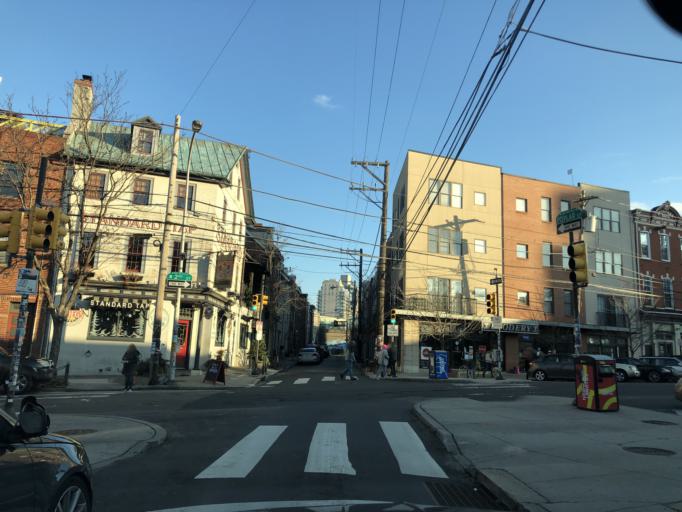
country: US
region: Pennsylvania
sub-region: Philadelphia County
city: Philadelphia
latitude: 39.9642
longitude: -75.1409
